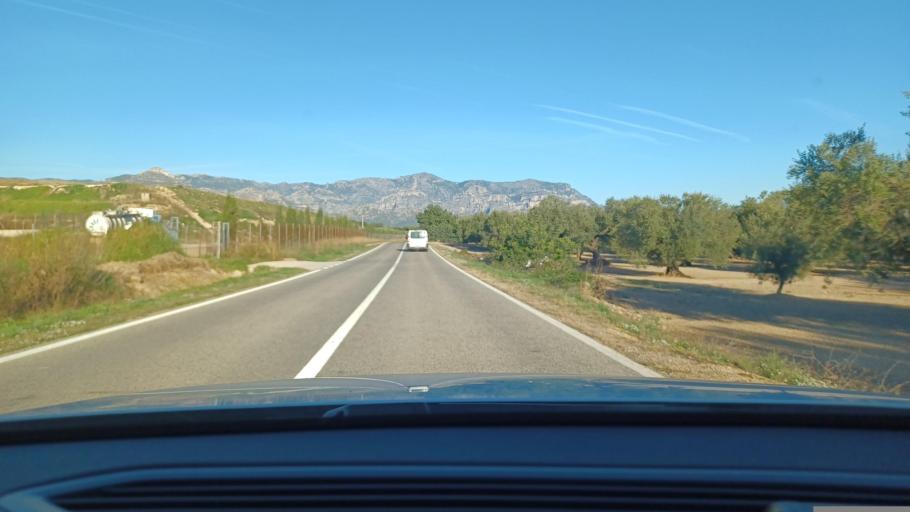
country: ES
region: Catalonia
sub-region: Provincia de Tarragona
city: Mas de Barberans
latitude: 40.7139
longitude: 0.4038
